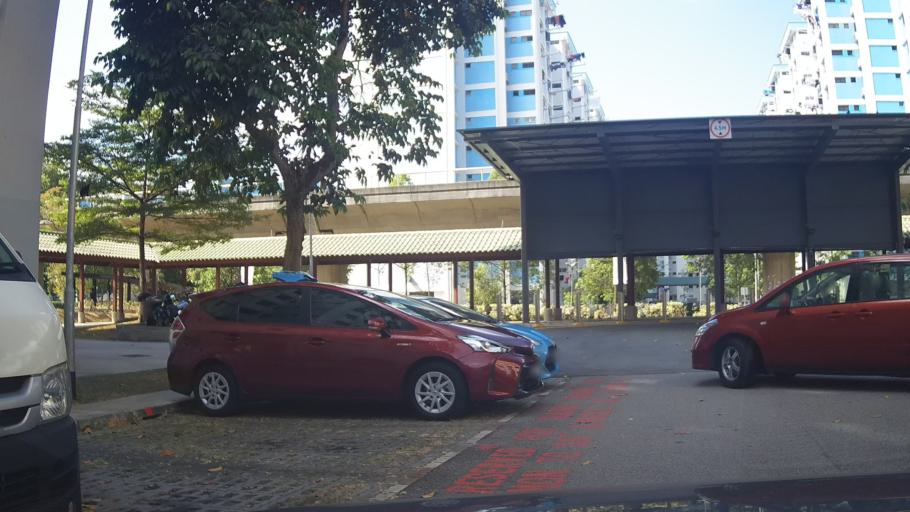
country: SG
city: Singapore
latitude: 1.3519
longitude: 103.9469
